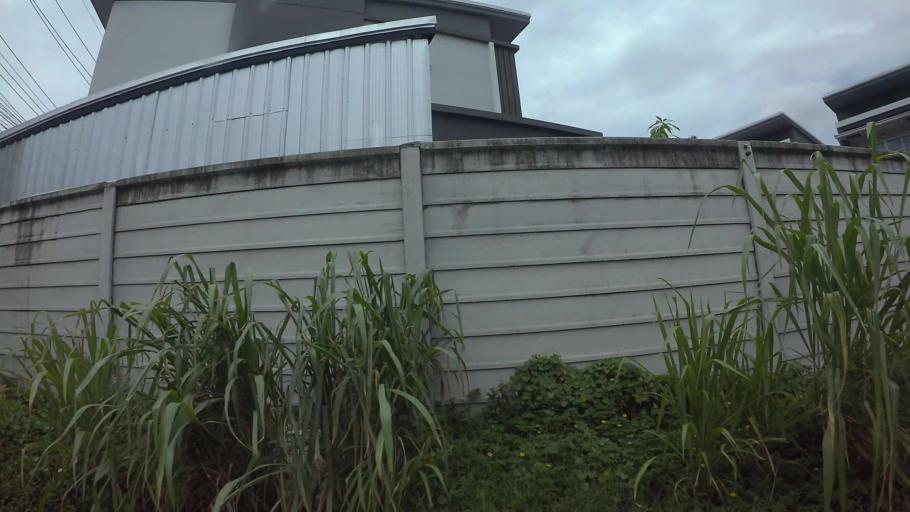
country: TH
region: Chon Buri
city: Si Racha
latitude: 13.1606
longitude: 100.9778
